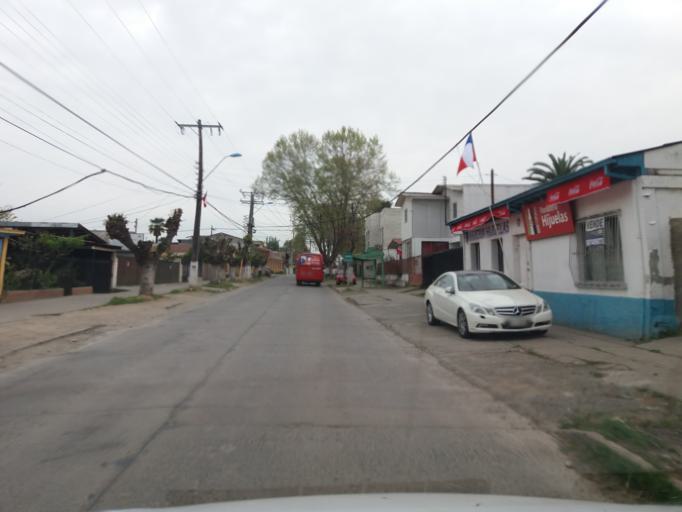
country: CL
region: Valparaiso
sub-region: Provincia de Quillota
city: Hacienda La Calera
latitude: -32.8029
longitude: -71.1438
